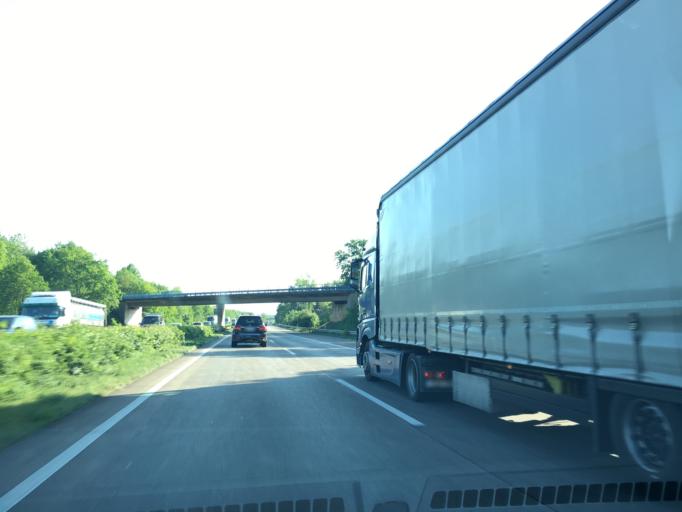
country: DE
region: North Rhine-Westphalia
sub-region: Regierungsbezirk Munster
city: Ladbergen
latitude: 52.1550
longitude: 7.7403
